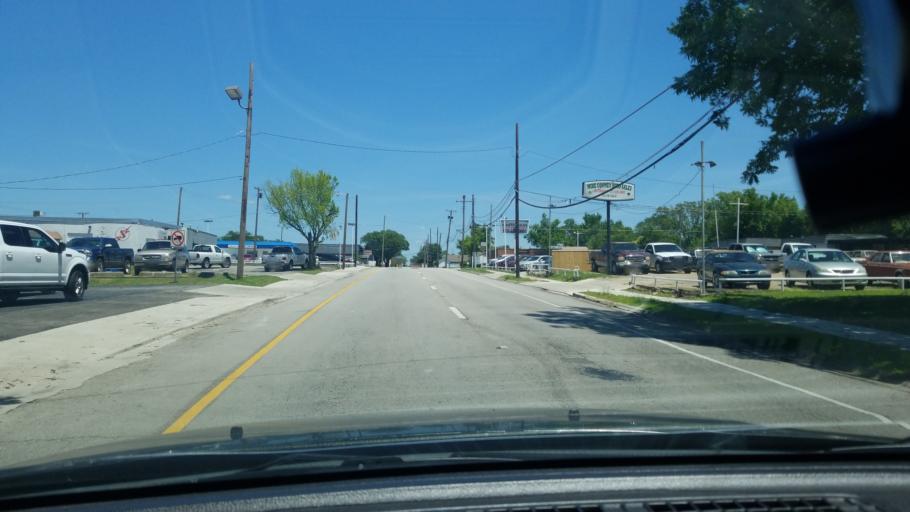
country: US
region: Texas
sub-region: Dallas County
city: Mesquite
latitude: 32.7668
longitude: -96.6054
